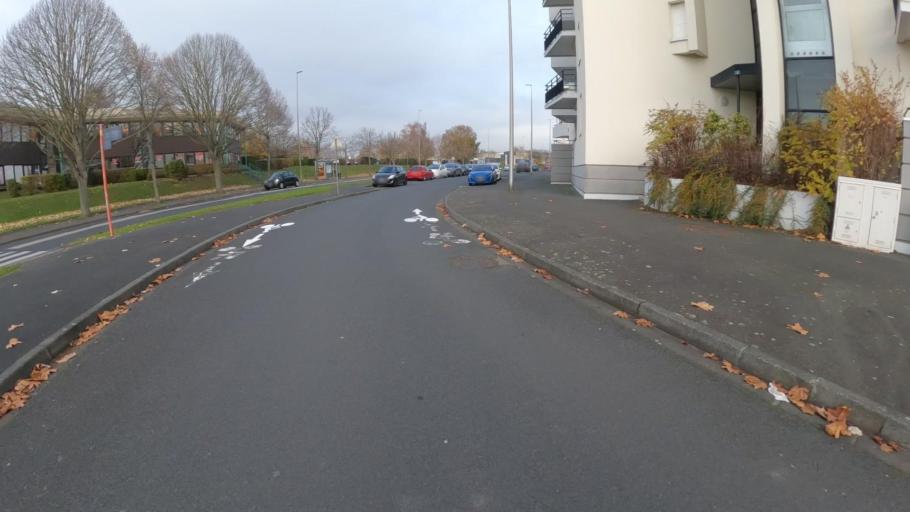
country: FR
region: Lower Normandy
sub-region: Departement du Calvados
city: Saint-Contest
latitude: 49.2013
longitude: -0.3877
